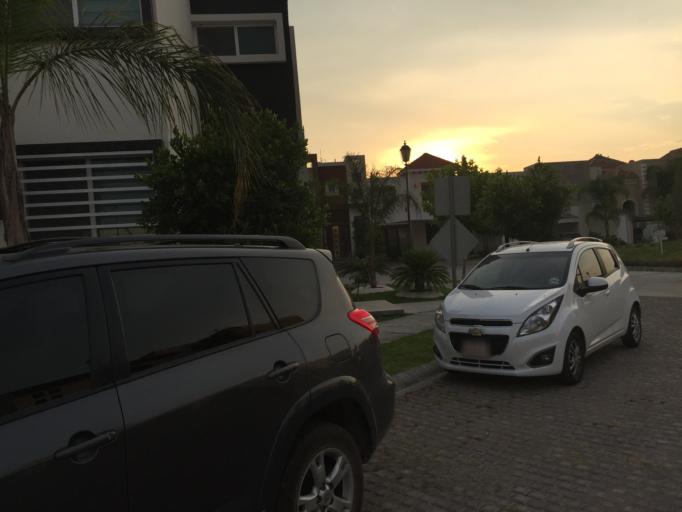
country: MX
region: Aguascalientes
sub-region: Aguascalientes
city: La Loma de los Negritos
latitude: 21.8458
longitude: -102.3557
